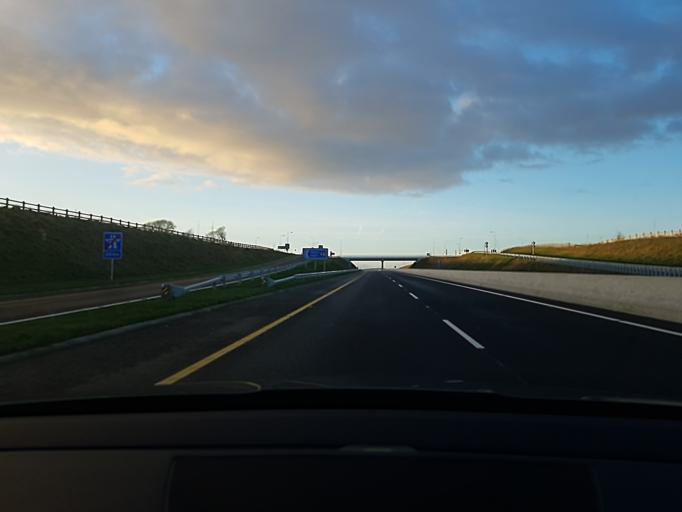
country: IE
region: Connaught
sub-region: County Galway
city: Tuam
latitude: 53.4012
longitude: -8.8148
